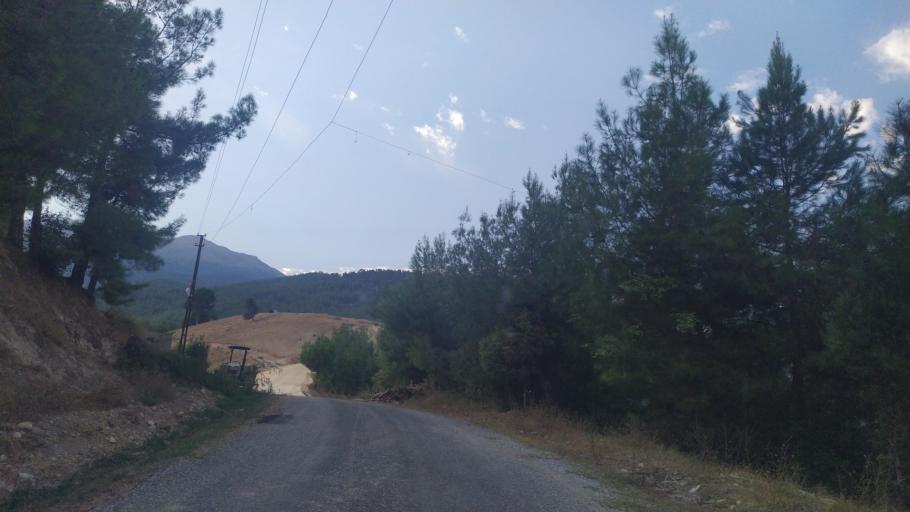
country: TR
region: Mersin
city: Camliyayla
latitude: 37.2255
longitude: 34.7106
